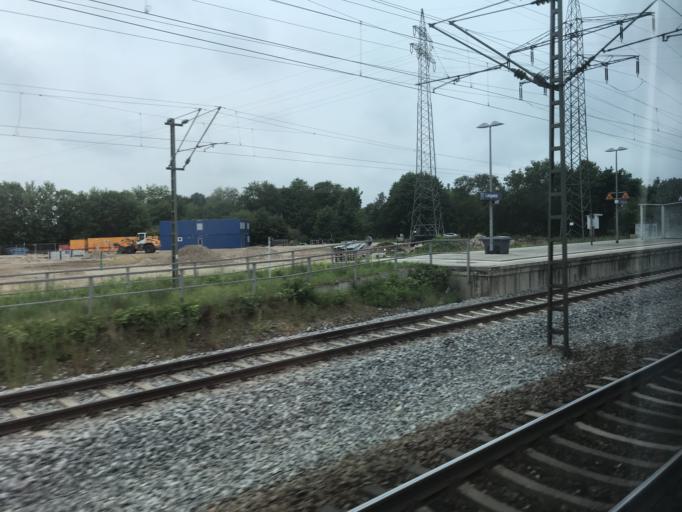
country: DE
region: Bavaria
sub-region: Upper Bavaria
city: Pasing
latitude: 48.1622
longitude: 11.4344
